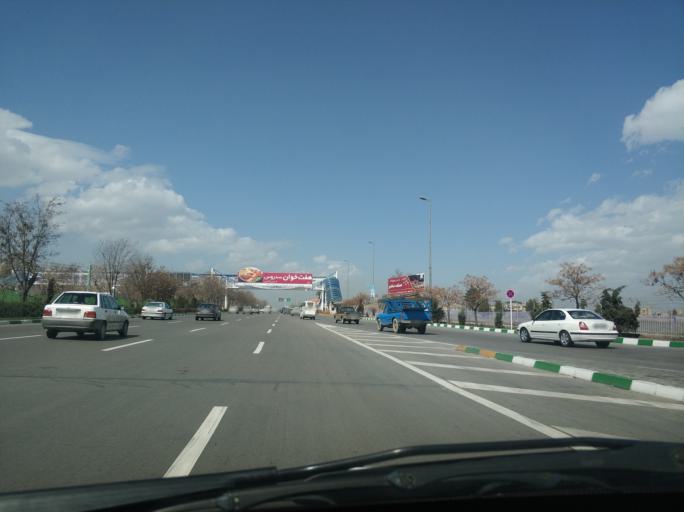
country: IR
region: Razavi Khorasan
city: Torqabeh
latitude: 36.3408
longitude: 59.4596
